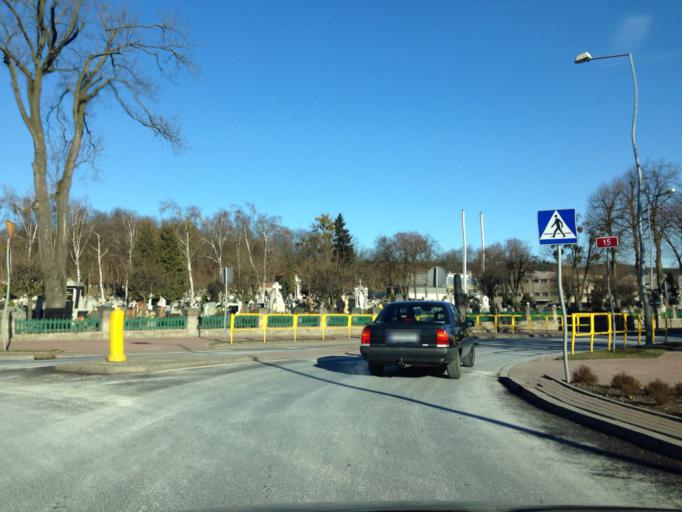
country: PL
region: Warmian-Masurian Voivodeship
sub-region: Powiat nowomiejski
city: Nowe Miasto Lubawskie
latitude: 53.4258
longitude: 19.5881
